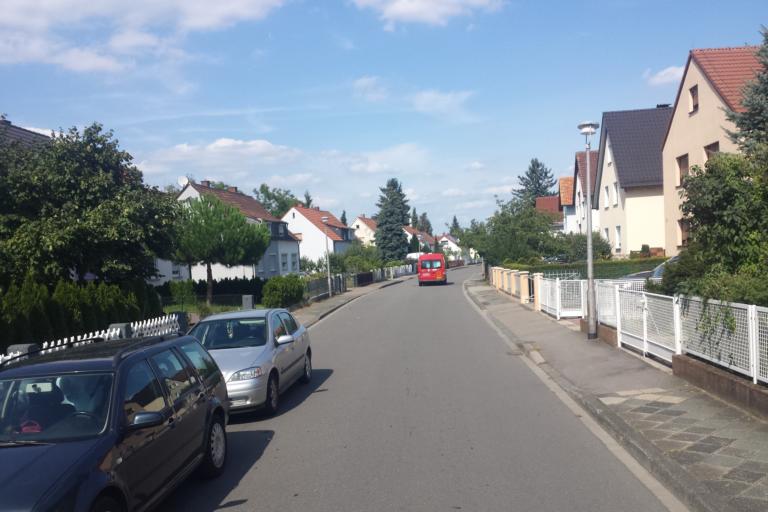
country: DE
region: Baden-Wuerttemberg
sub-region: Karlsruhe Region
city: Mannheim
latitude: 49.5196
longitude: 8.5024
